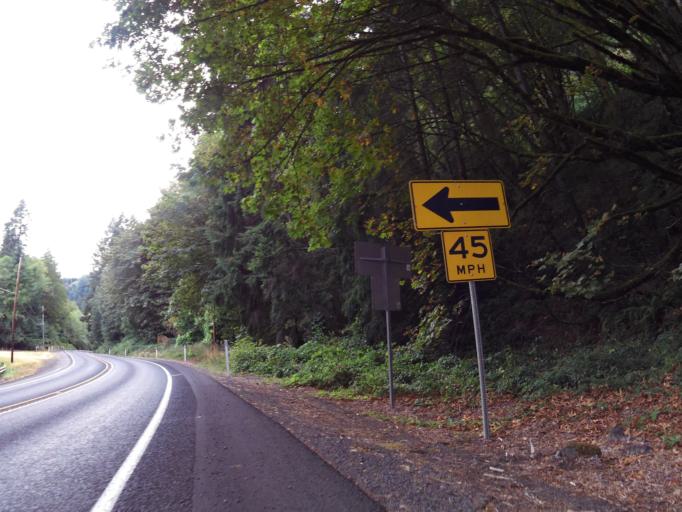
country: US
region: Oregon
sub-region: Columbia County
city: Clatskanie
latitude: 46.1733
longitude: -123.2269
